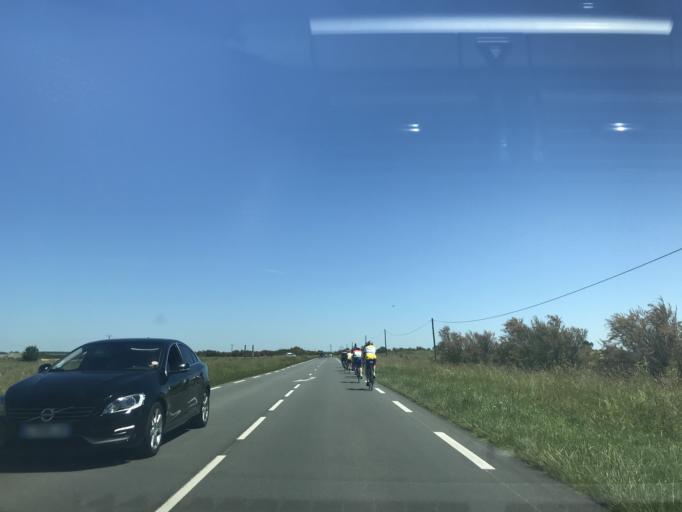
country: FR
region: Poitou-Charentes
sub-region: Departement de la Charente-Maritime
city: Meschers-sur-Gironde
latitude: 45.5609
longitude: -0.9335
